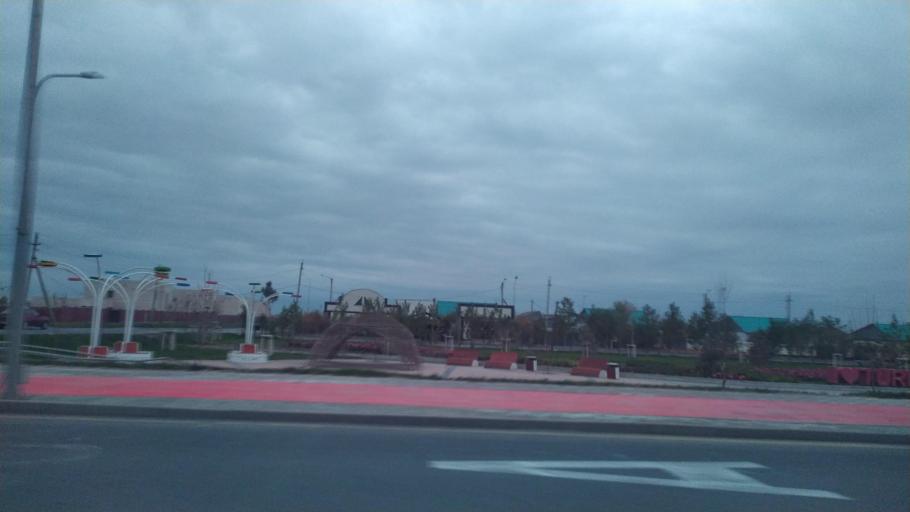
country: KZ
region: Ongtustik Qazaqstan
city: Turkestan
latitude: 43.2773
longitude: 68.3298
